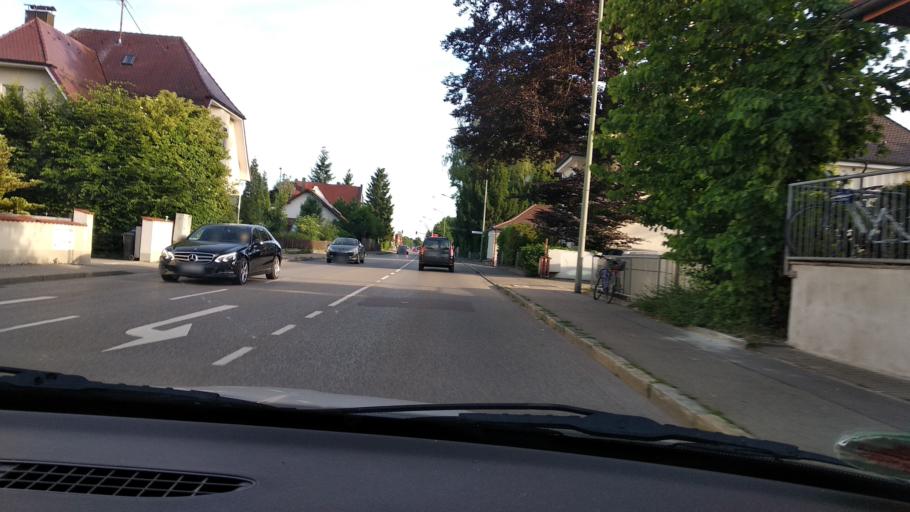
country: DE
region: Bavaria
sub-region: Swabia
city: Illertissen
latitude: 48.2201
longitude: 10.1025
